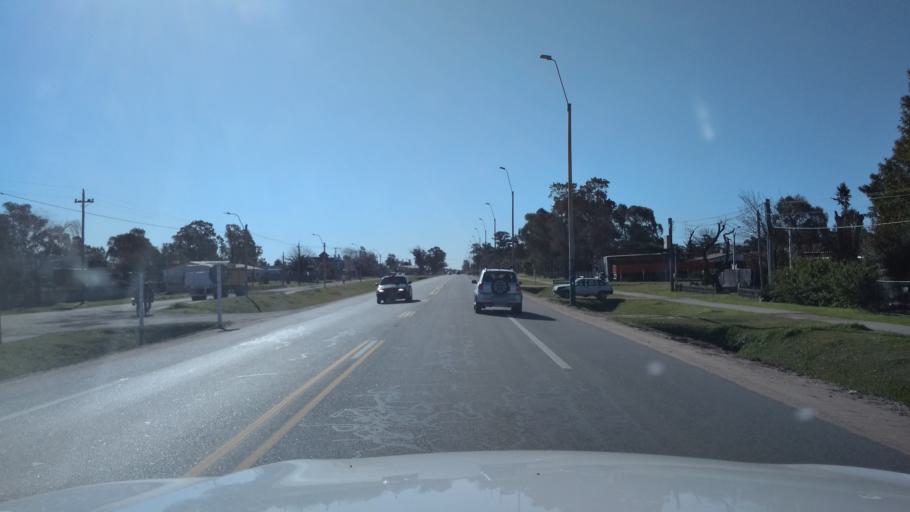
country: UY
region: Canelones
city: Atlantida
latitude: -34.7608
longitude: -55.7656
